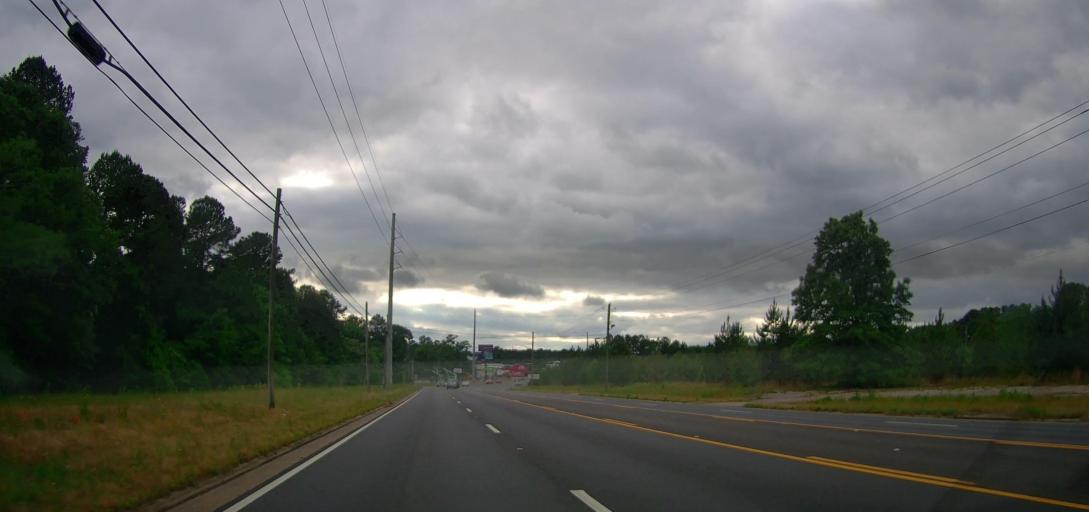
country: US
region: Georgia
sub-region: Oconee County
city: Bogart
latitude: 33.9400
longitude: -83.4914
